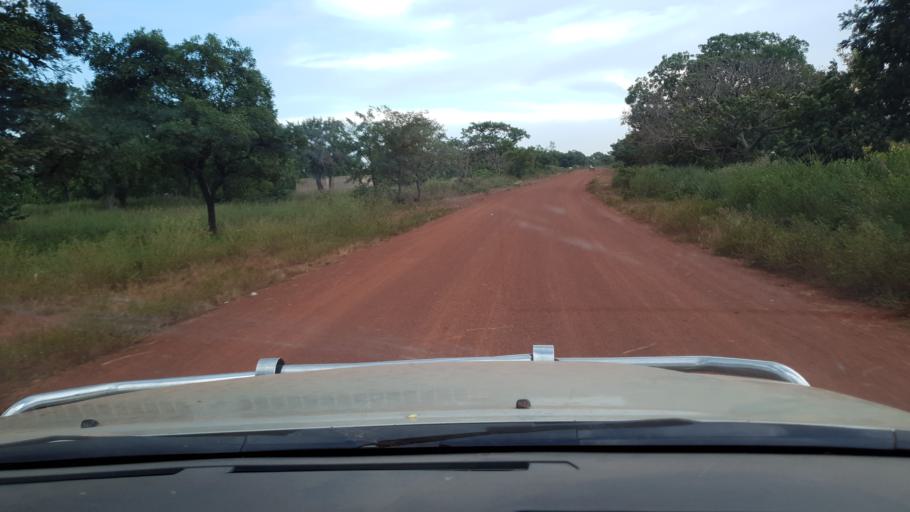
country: ML
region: Sikasso
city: Kolondieba
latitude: 11.4433
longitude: -6.3399
